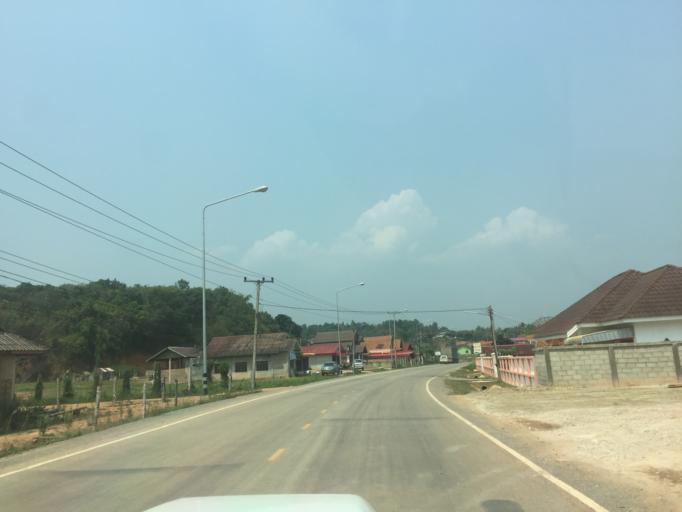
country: TH
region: Nan
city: Thung Chang
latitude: 19.6326
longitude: 100.8120
